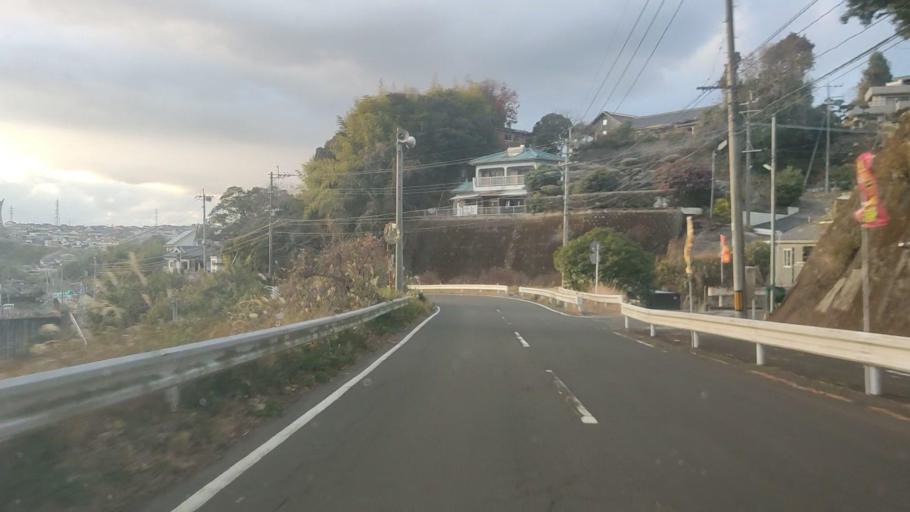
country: JP
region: Kagoshima
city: Kagoshima-shi
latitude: 31.6272
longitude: 130.5513
